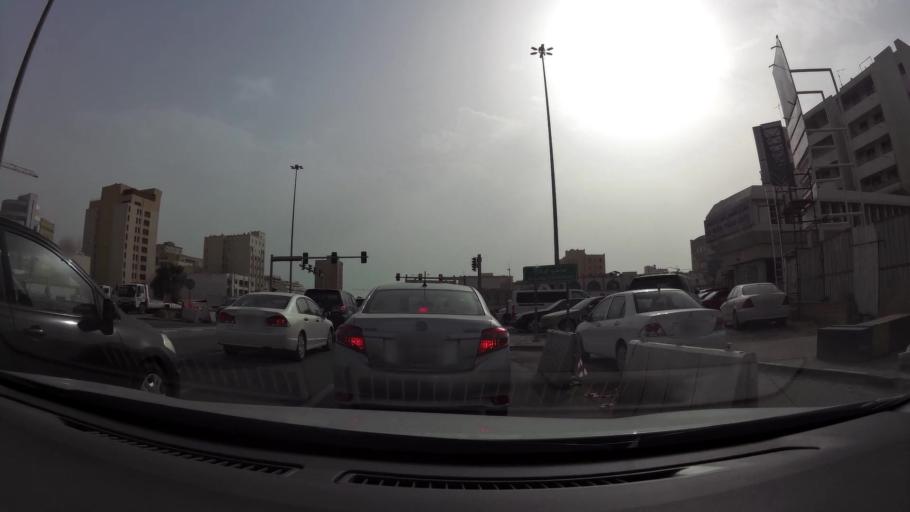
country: QA
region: Baladiyat ad Dawhah
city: Doha
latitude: 25.2826
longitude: 51.5438
